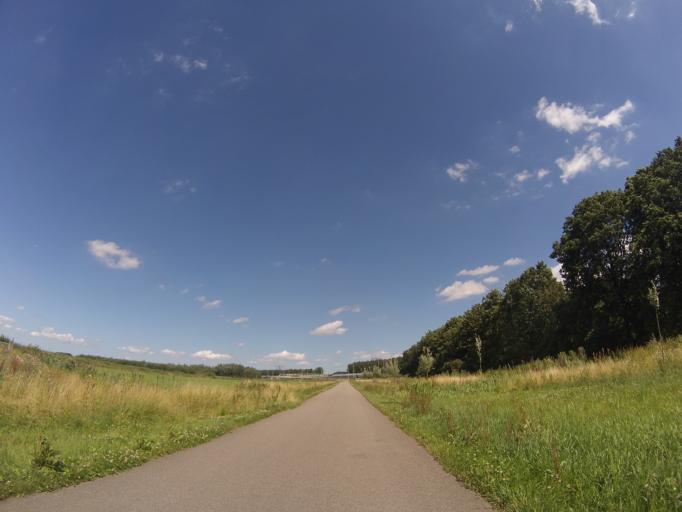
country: NL
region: Utrecht
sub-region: Stichtse Vecht
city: Spechtenkamp
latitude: 52.1339
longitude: 5.0047
